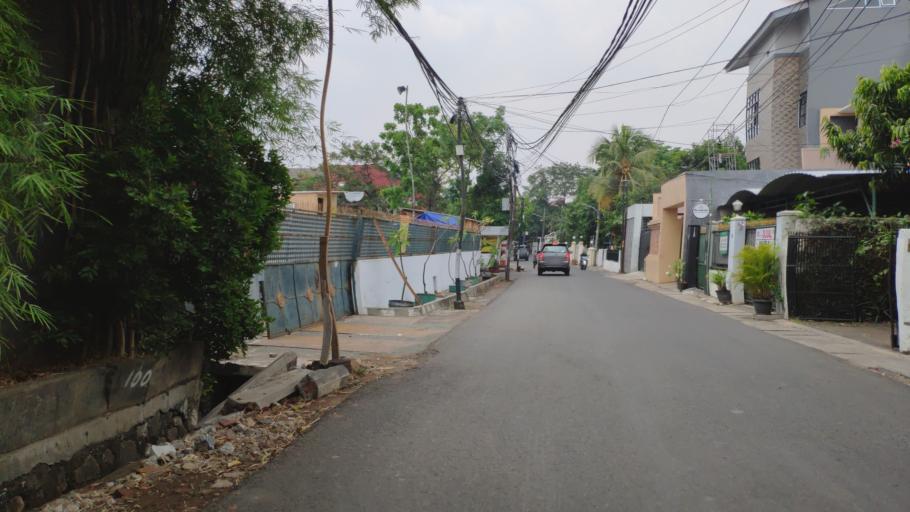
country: ID
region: Jakarta Raya
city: Jakarta
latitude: -6.2676
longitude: 106.7964
